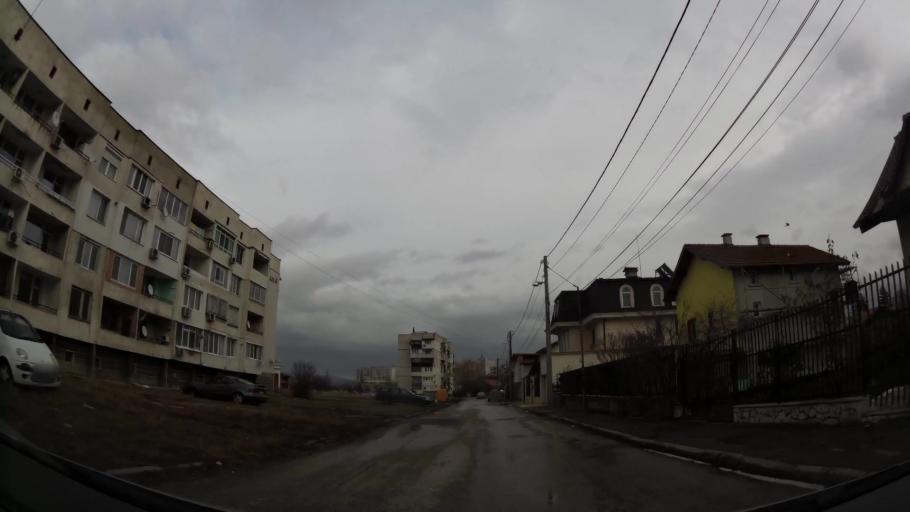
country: BG
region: Sofiya
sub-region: Obshtina Bozhurishte
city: Bozhurishte
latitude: 42.7455
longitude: 23.2635
